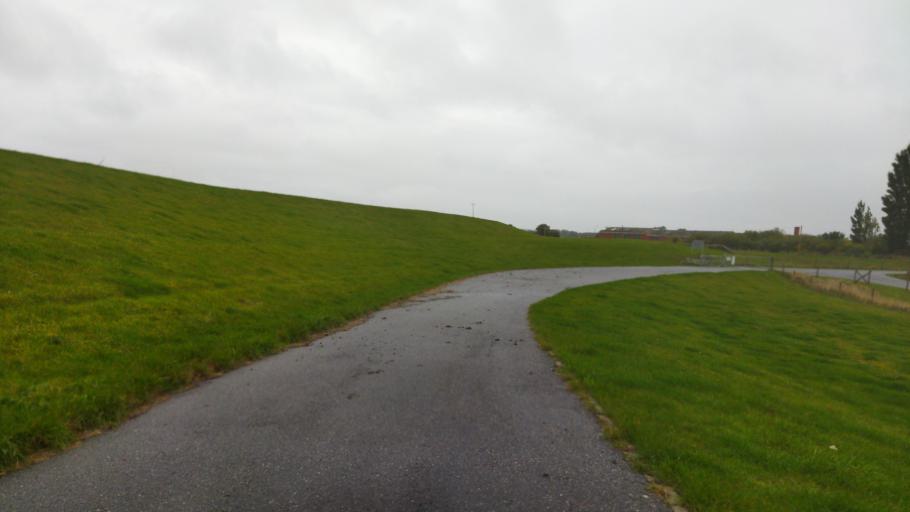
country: NL
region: Groningen
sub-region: Gemeente Delfzijl
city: Delfzijl
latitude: 53.3375
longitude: 7.0546
